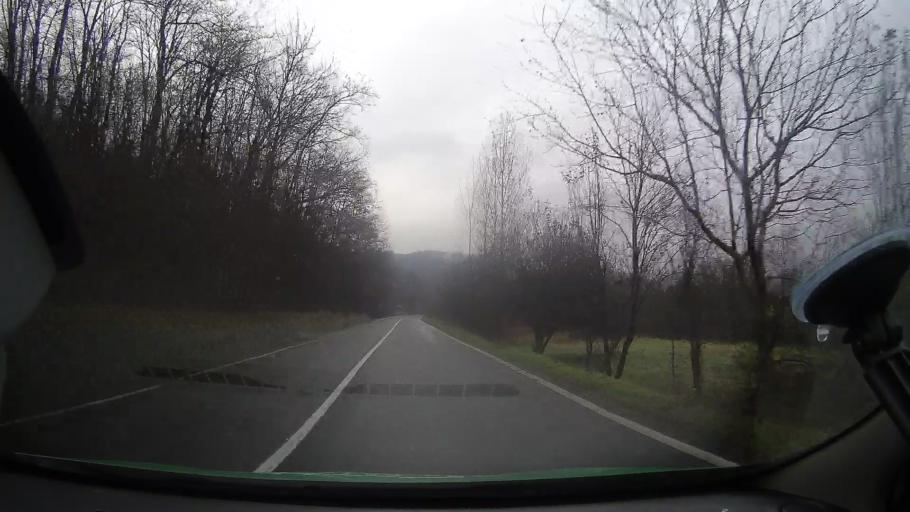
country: RO
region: Arad
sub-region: Comuna Gurahont
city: Gurahont
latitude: 46.2893
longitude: 22.3880
